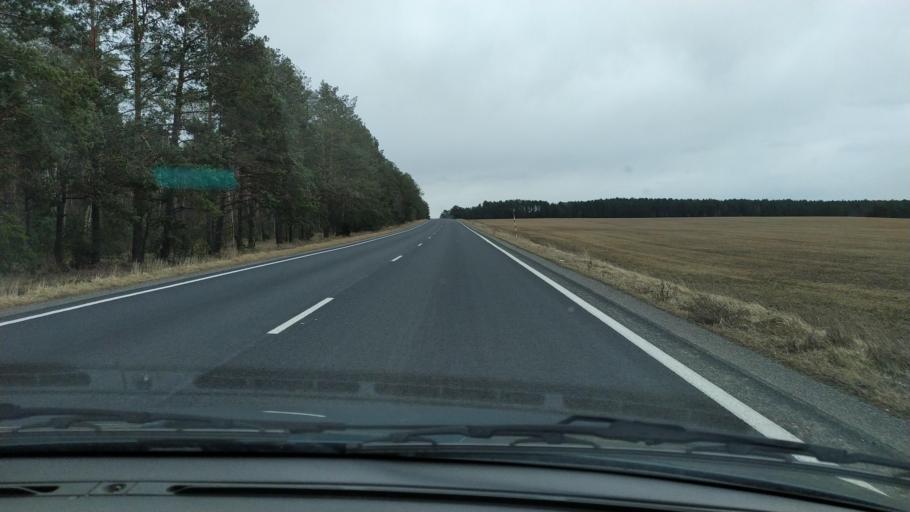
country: BY
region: Brest
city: Kamyanyets
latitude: 52.3974
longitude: 23.9132
